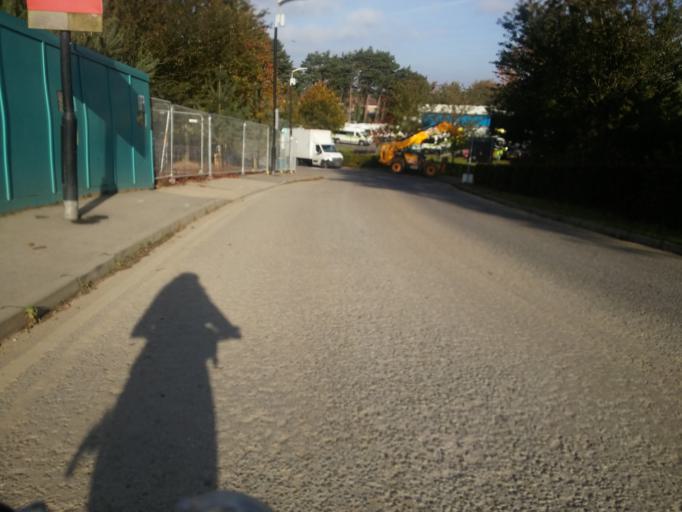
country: GB
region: Northern Ireland
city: Londonderry County Borough
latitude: 54.9870
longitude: -7.2896
